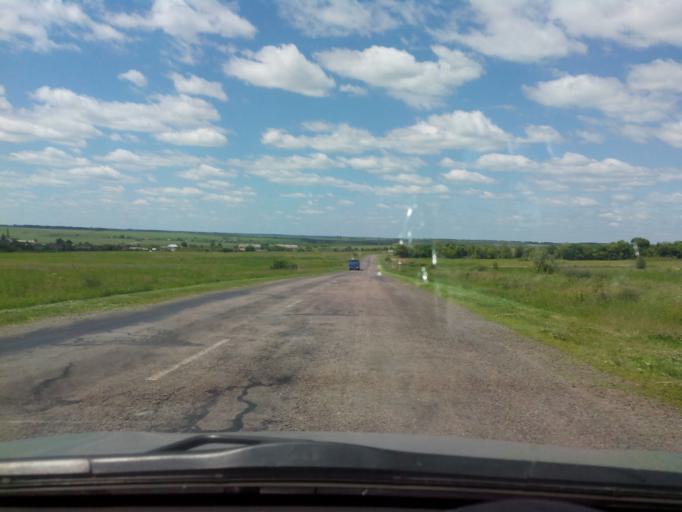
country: RU
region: Voronezj
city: Ternovka
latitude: 51.5932
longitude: 41.8023
